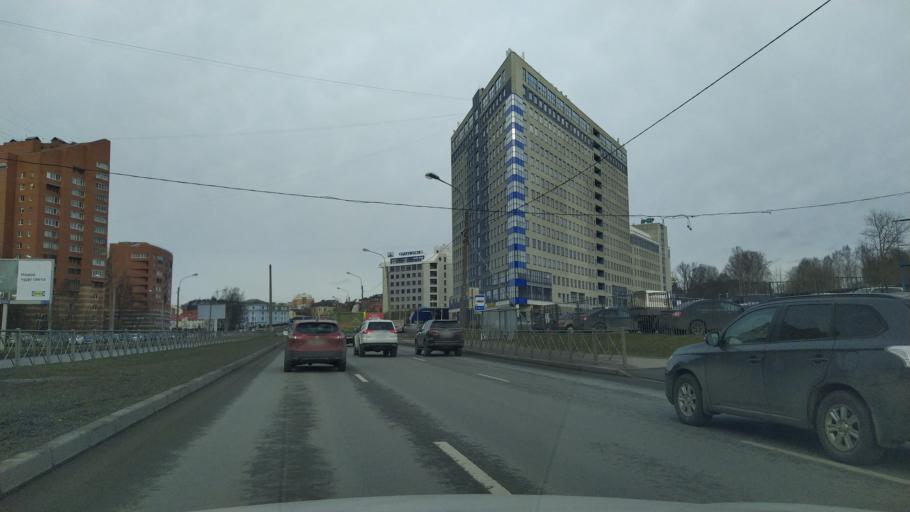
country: RU
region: St.-Petersburg
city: Kolomyagi
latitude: 60.0121
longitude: 30.2949
